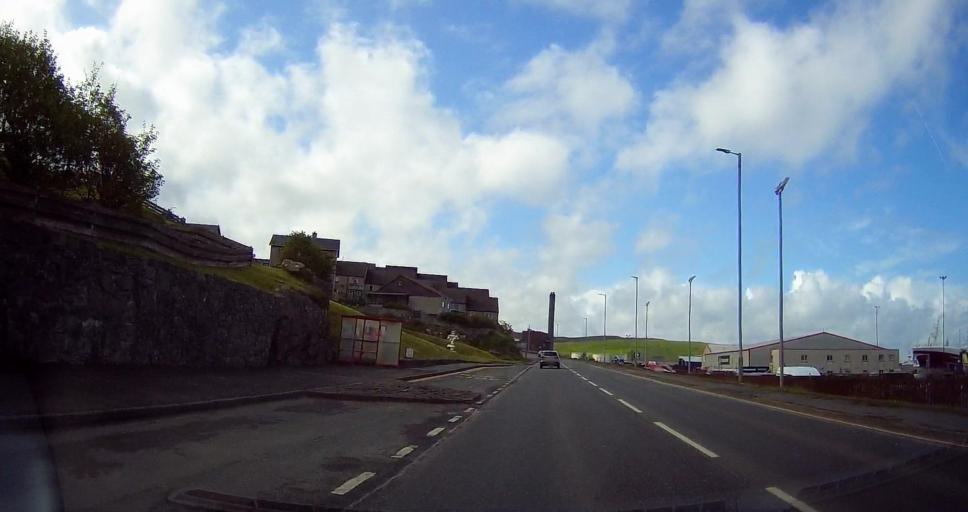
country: GB
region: Scotland
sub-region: Shetland Islands
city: Lerwick
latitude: 60.1623
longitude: -1.1591
